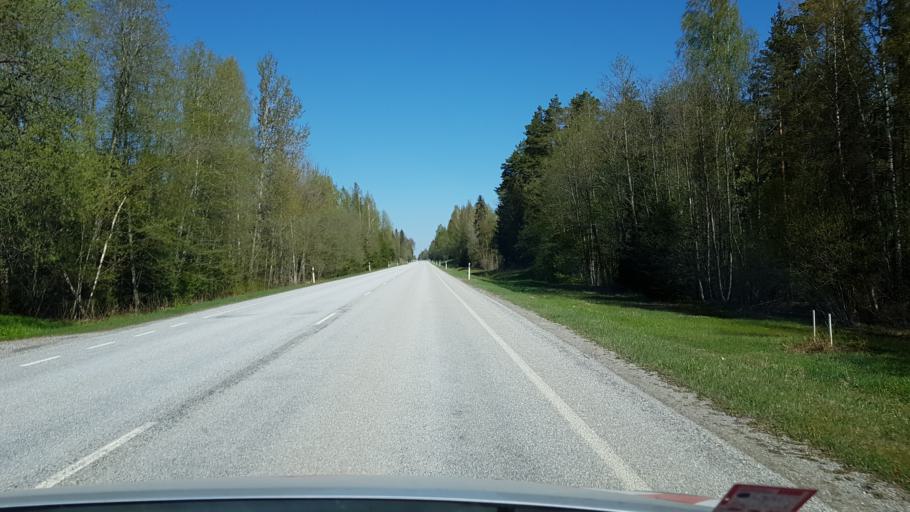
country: RU
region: Pskov
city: Pechory
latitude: 57.6621
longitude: 27.3308
